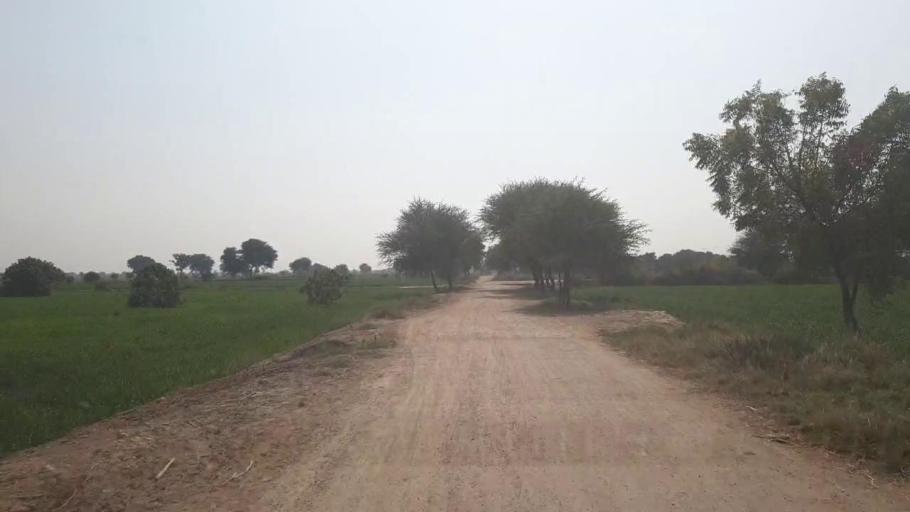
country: PK
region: Sindh
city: Tando Allahyar
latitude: 25.4765
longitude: 68.8350
